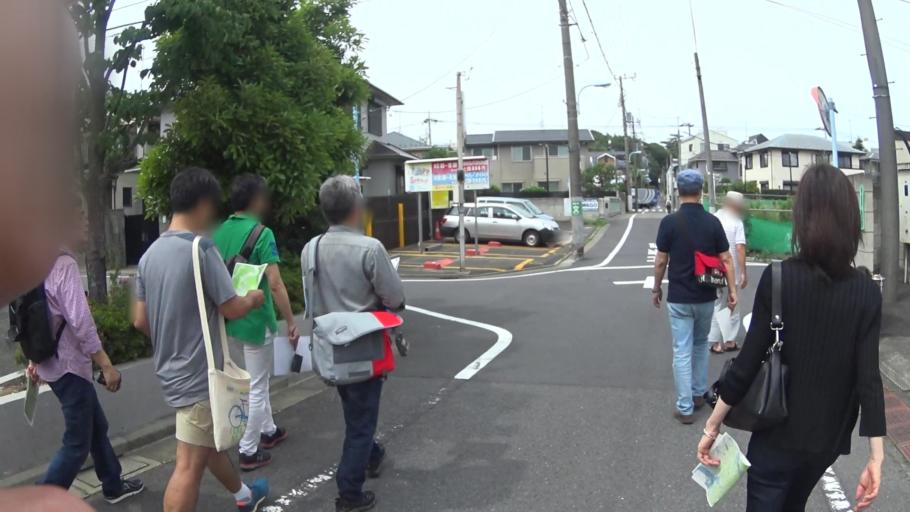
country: JP
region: Tokyo
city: Musashino
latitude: 35.7083
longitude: 139.6057
